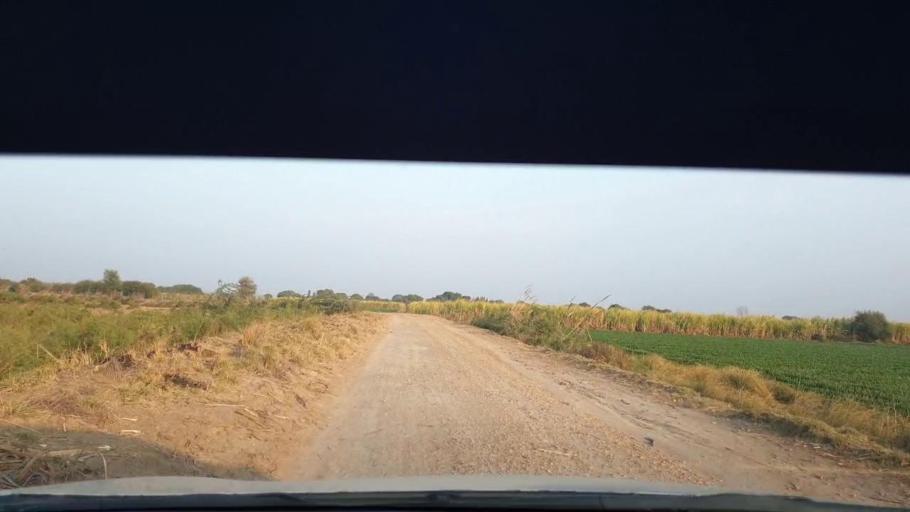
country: PK
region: Sindh
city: Berani
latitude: 25.7400
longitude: 68.9660
